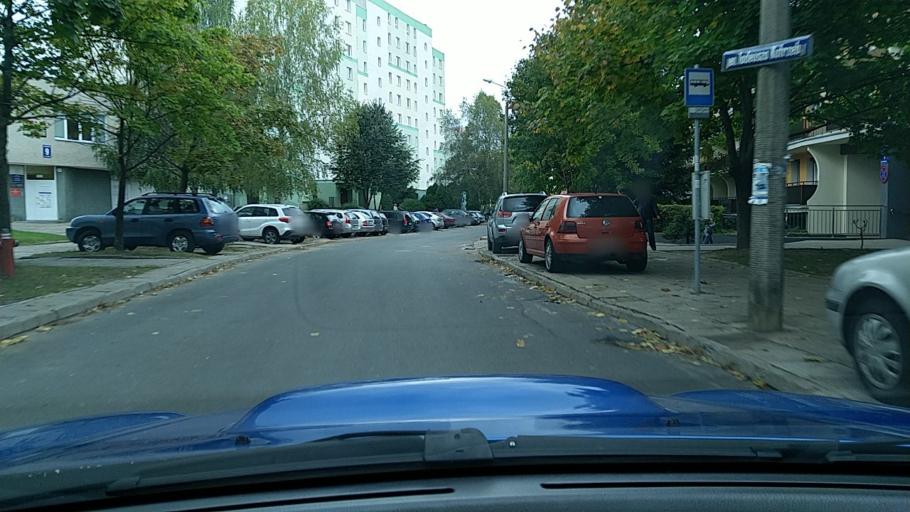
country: PL
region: Warmian-Masurian Voivodeship
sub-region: Olsztyn
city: Kortowo
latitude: 53.7415
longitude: 20.4816
